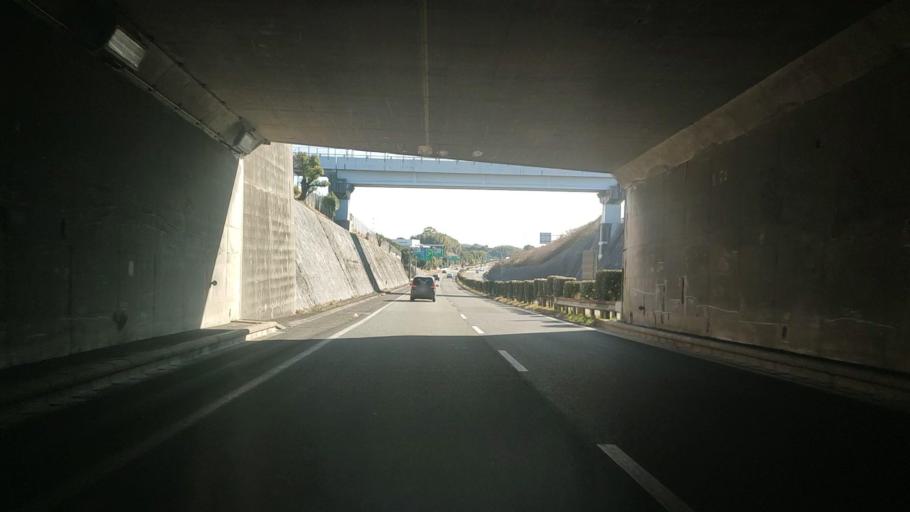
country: JP
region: Fukuoka
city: Nakama
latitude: 33.7923
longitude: 130.7449
